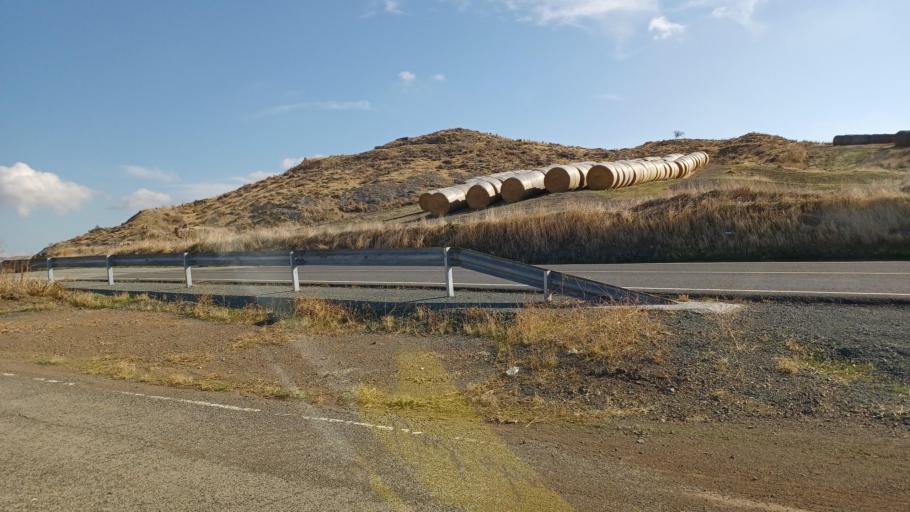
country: CY
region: Larnaka
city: Troulloi
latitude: 35.0172
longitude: 33.5857
